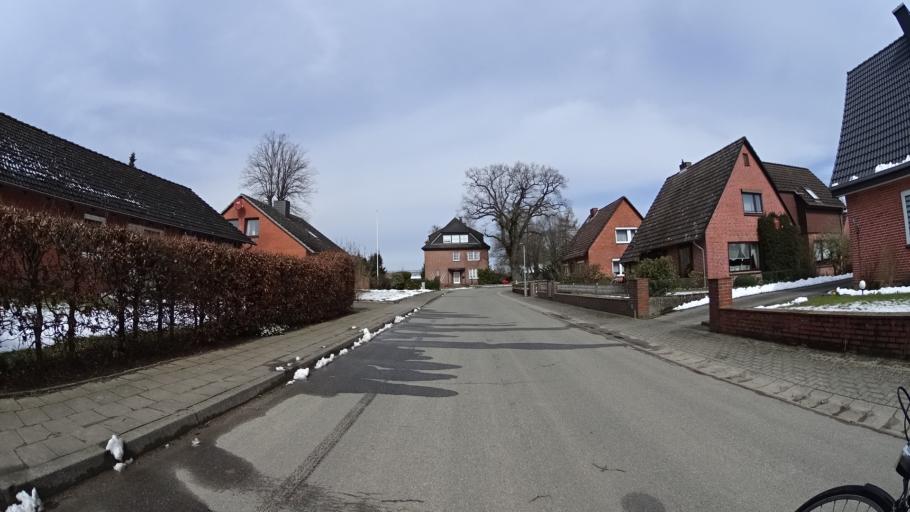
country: DE
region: Schleswig-Holstein
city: Rendswuhren
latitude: 54.0842
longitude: 10.1984
